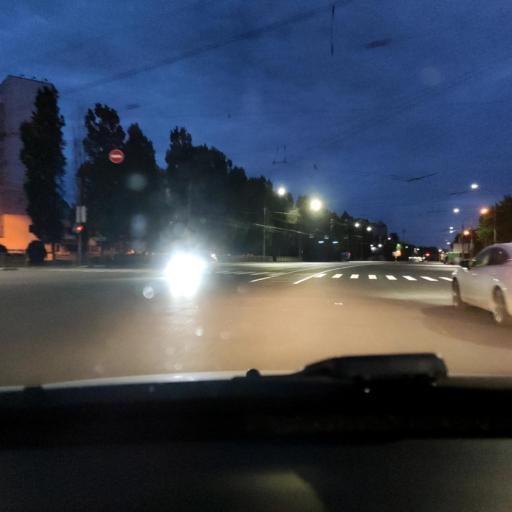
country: RU
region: Voronezj
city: Voronezh
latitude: 51.6462
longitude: 39.1595
